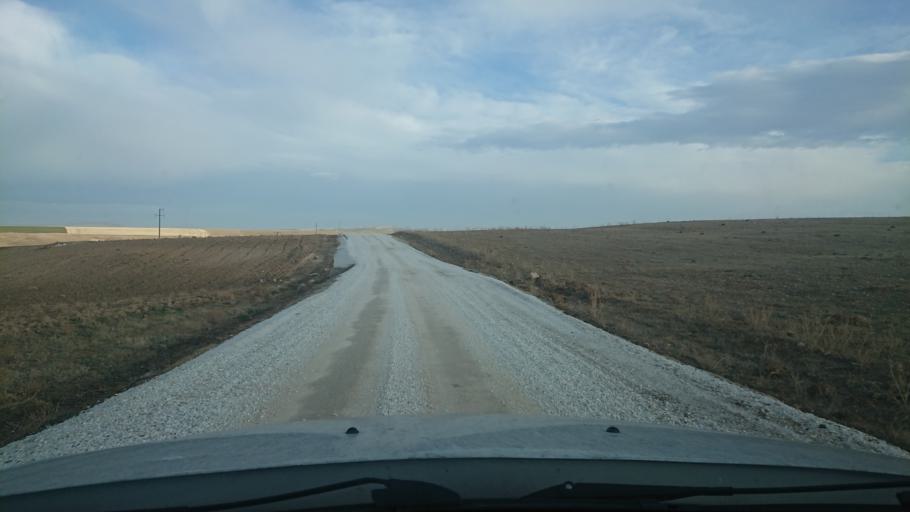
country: TR
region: Aksaray
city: Agacoren
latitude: 38.7352
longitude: 33.8695
